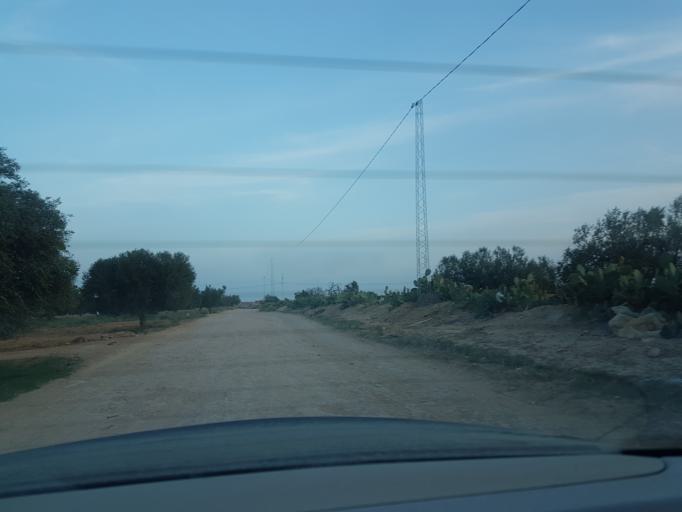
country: TN
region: Safaqis
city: Sfax
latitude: 34.7042
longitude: 10.6931
